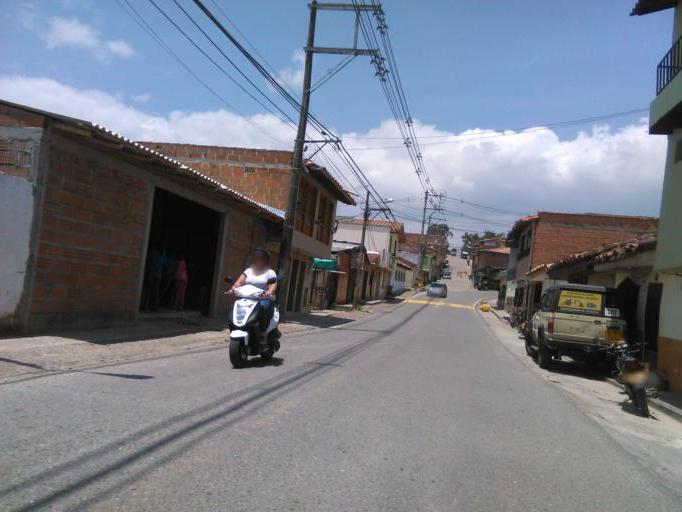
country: CO
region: Antioquia
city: La Union
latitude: 5.9763
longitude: -75.3627
